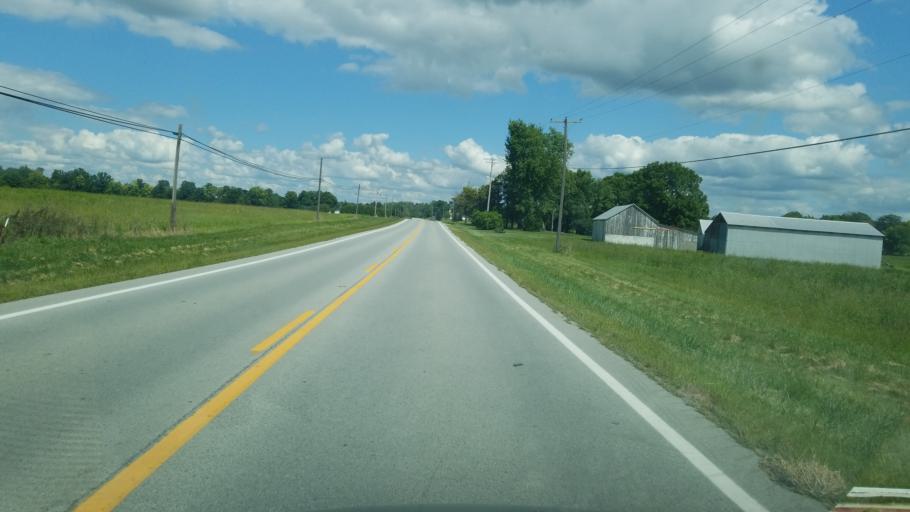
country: US
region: Ohio
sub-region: Allen County
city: Lima
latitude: 40.7611
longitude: -84.0396
